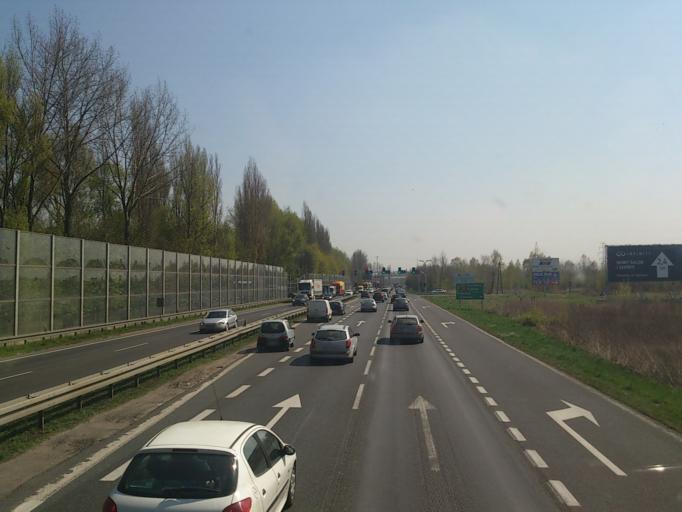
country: PL
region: Silesian Voivodeship
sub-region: Powiat bedzinski
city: Bedzin
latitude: 50.3154
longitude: 19.1096
